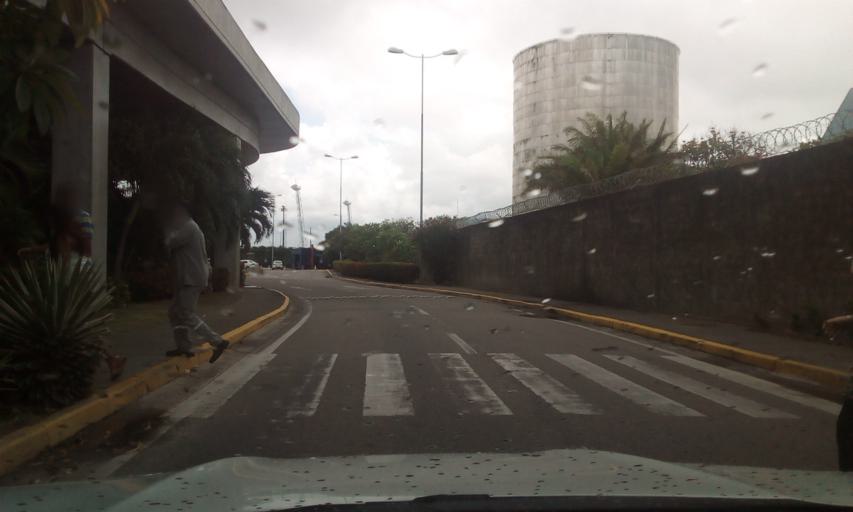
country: BR
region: Pernambuco
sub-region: Recife
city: Recife
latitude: -8.1304
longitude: -34.9177
